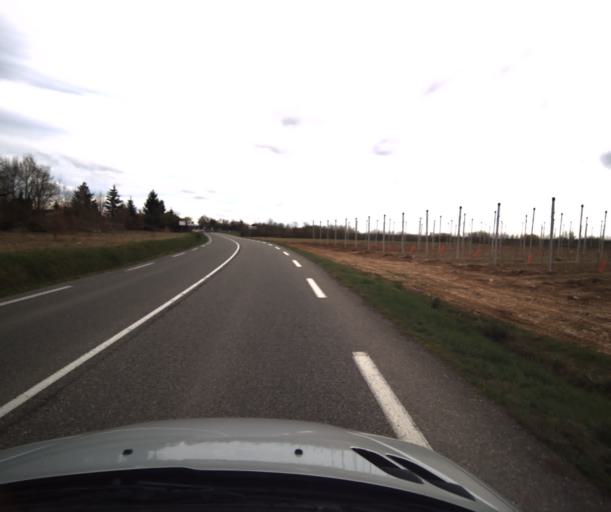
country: FR
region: Midi-Pyrenees
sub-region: Departement du Tarn-et-Garonne
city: Montbeton
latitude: 44.0361
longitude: 1.3110
